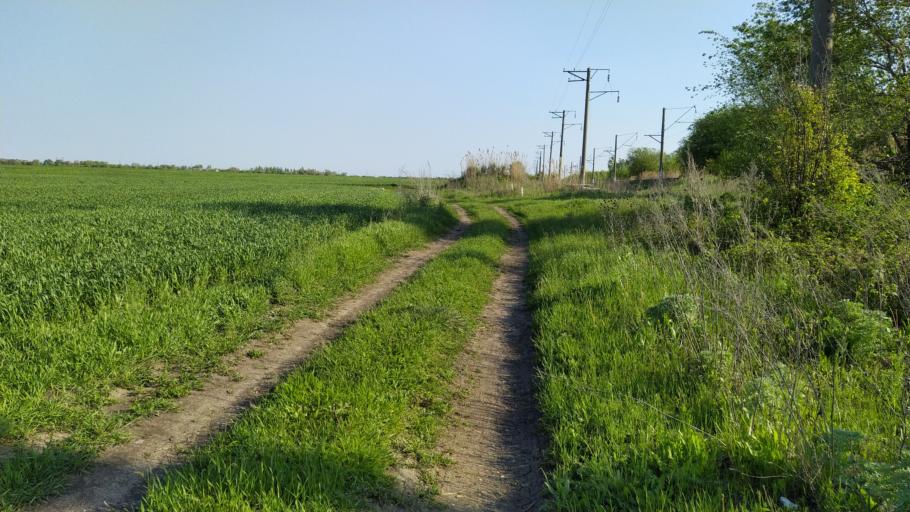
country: RU
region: Rostov
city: Bataysk
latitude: 47.1146
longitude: 39.7138
